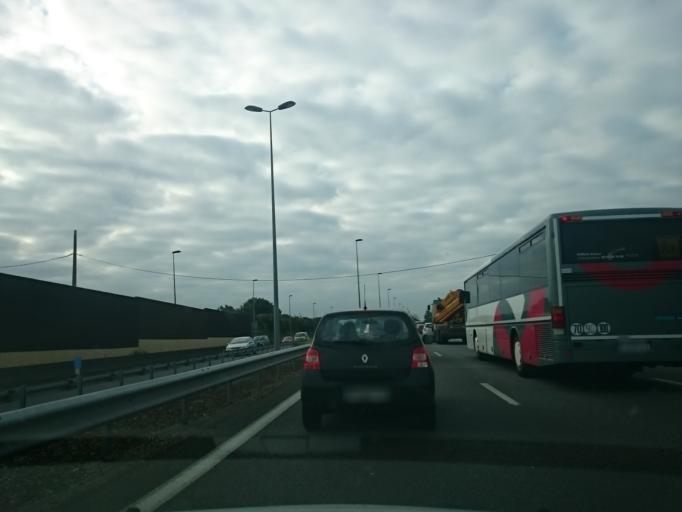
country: FR
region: Brittany
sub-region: Departement du Finistere
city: Le Relecq-Kerhuon
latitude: 48.4141
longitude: -4.4219
